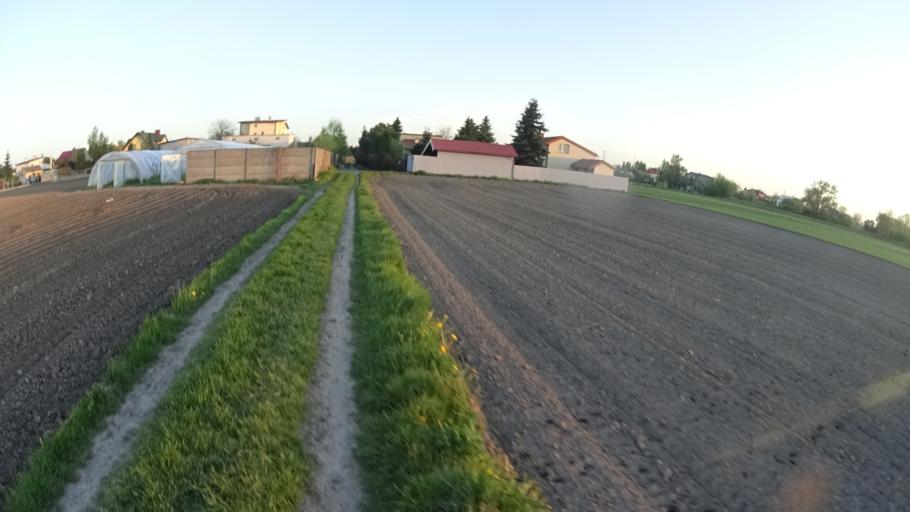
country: PL
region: Masovian Voivodeship
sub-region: Powiat warszawski zachodni
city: Ozarow Mazowiecki
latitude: 52.2240
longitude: 20.7811
